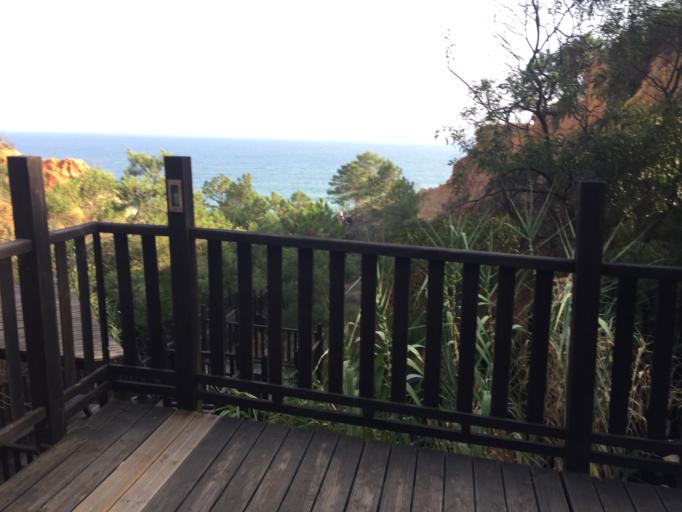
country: PT
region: Faro
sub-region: Loule
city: Boliqueime
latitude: 37.0915
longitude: -8.1864
